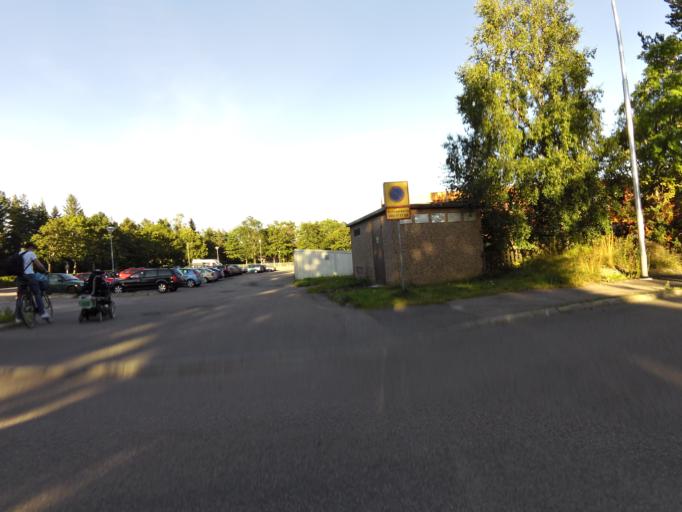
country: SE
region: Gaevleborg
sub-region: Gavle Kommun
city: Gavle
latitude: 60.6556
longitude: 17.1347
